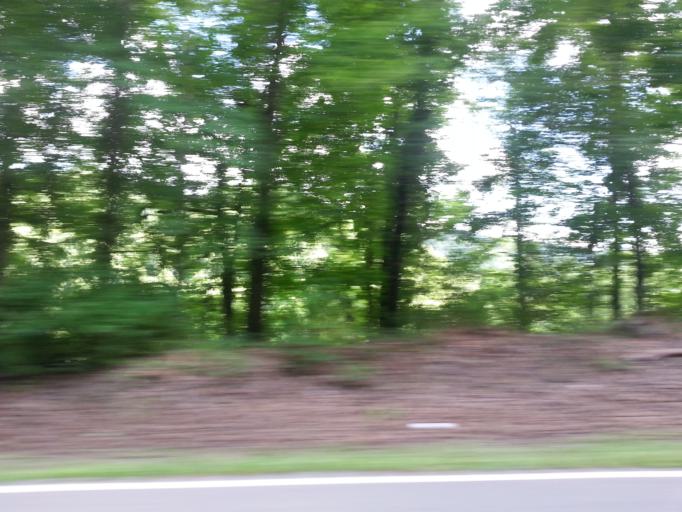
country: US
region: Kentucky
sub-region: Harlan County
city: Harlan
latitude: 36.8950
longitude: -83.2692
